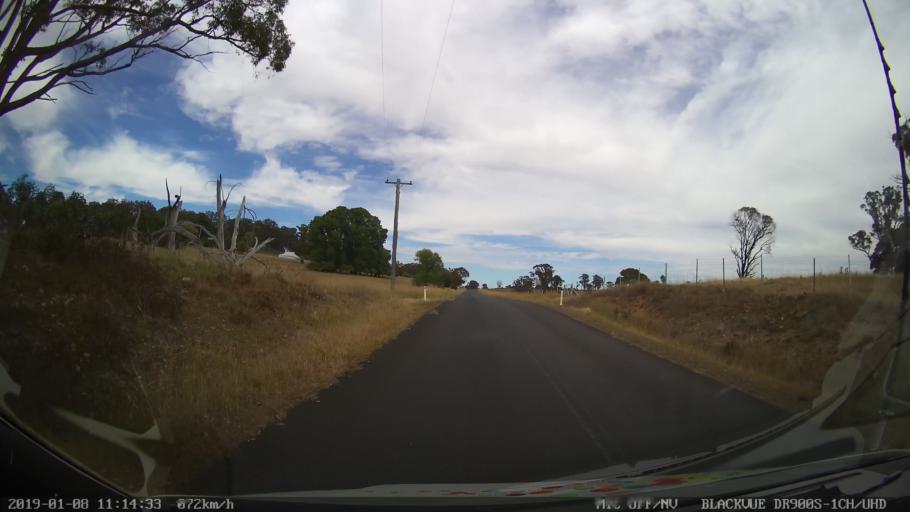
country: AU
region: New South Wales
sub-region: Guyra
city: Guyra
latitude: -30.2253
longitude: 151.5882
